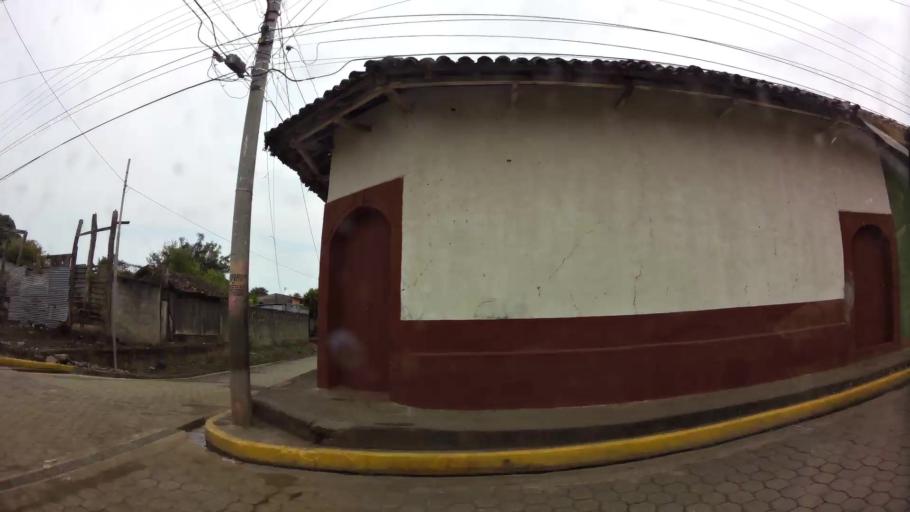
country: NI
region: Granada
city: Nandaime
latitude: 11.7561
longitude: -86.0494
